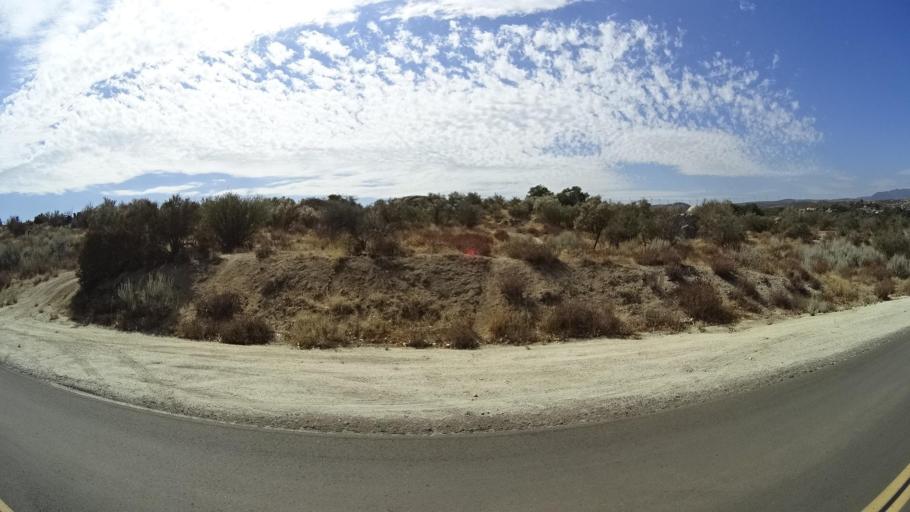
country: US
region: California
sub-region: San Diego County
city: Campo
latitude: 32.6961
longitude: -116.2933
